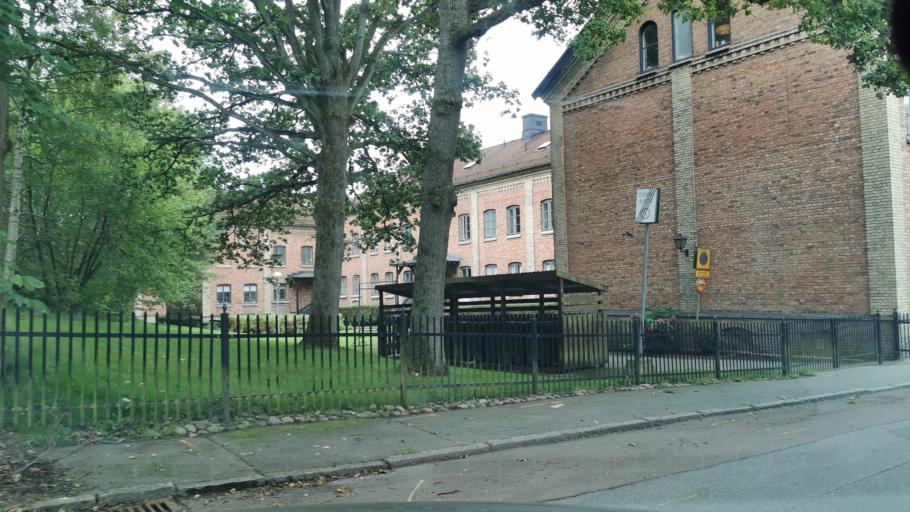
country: SE
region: Vaestra Goetaland
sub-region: Goteborg
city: Goeteborg
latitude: 57.6926
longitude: 11.9617
